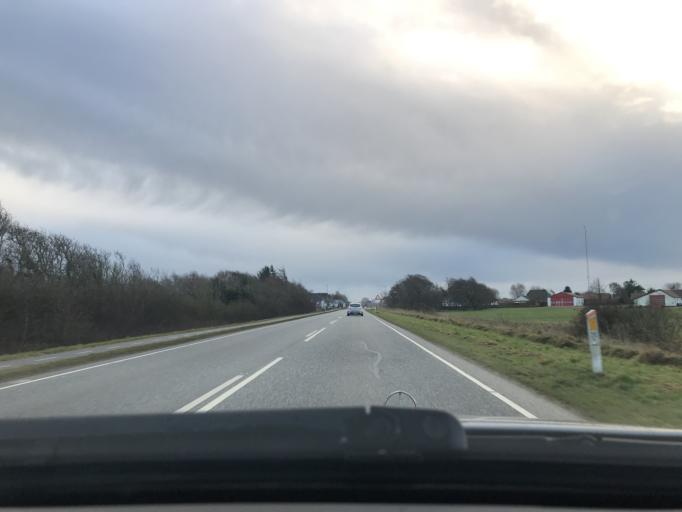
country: DK
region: South Denmark
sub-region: Tonder Kommune
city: Sherrebek
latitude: 55.2356
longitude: 8.7241
